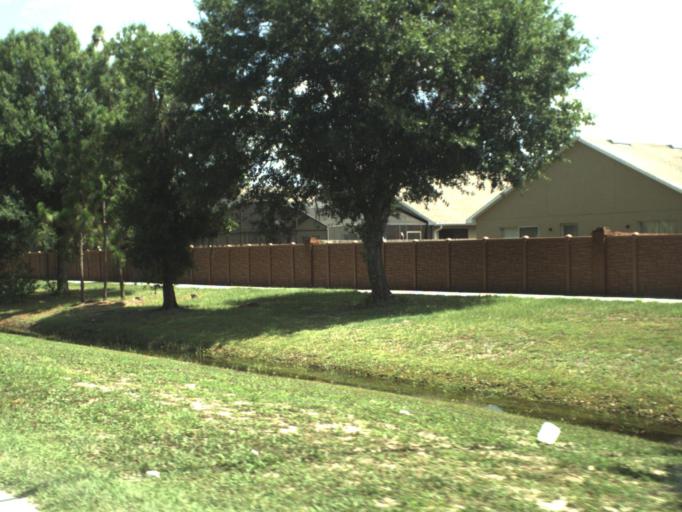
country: US
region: Florida
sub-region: Orange County
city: Conway
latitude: 28.4734
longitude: -81.2812
